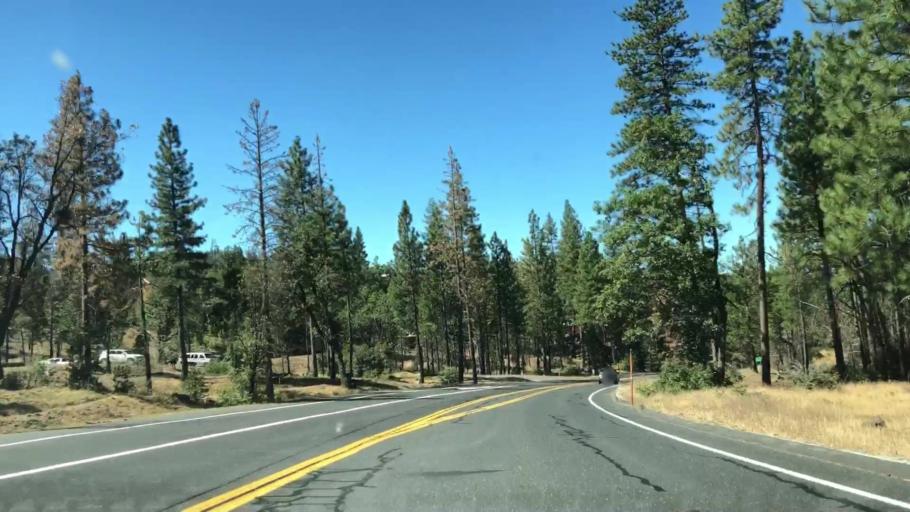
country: US
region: California
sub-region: Mariposa County
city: Midpines
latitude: 37.8141
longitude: -119.8801
